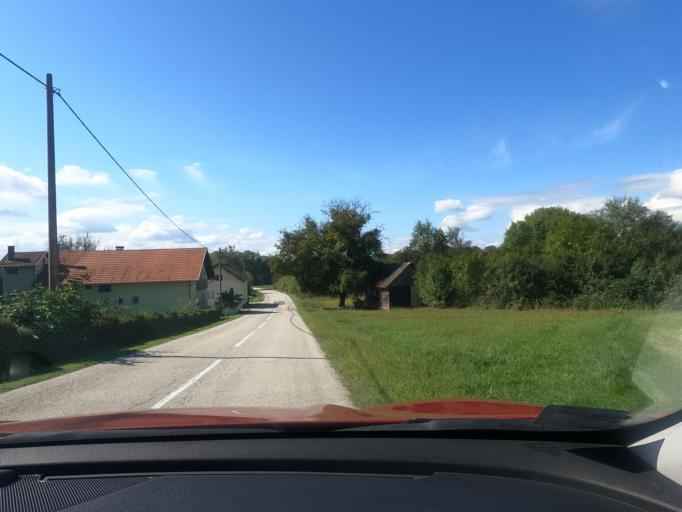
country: BA
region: Federation of Bosnia and Herzegovina
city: Vrnograc
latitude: 45.2590
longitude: 15.9490
